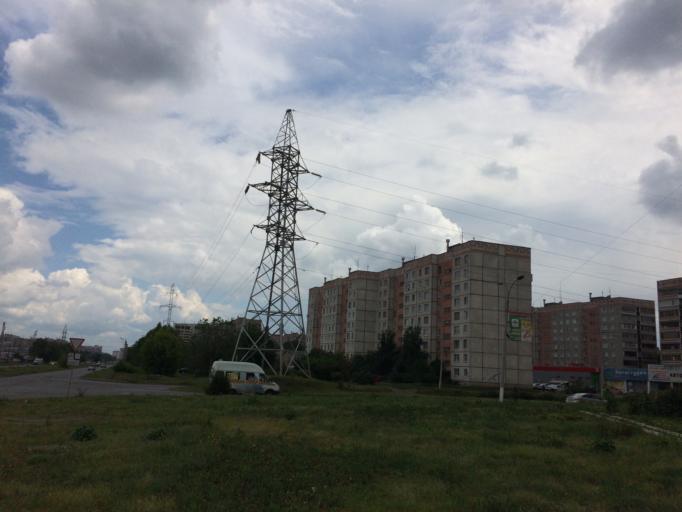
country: RU
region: Chelyabinsk
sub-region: Gorod Magnitogorsk
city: Magnitogorsk
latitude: 53.3647
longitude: 58.9503
